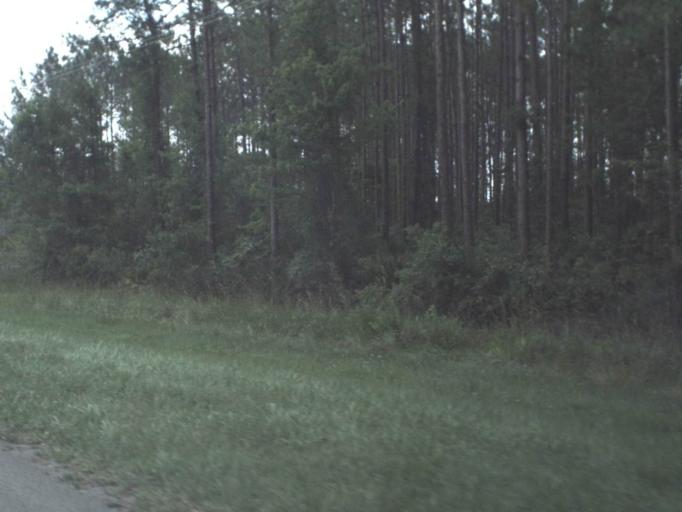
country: US
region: Florida
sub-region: Duval County
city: Baldwin
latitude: 30.2346
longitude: -82.0018
